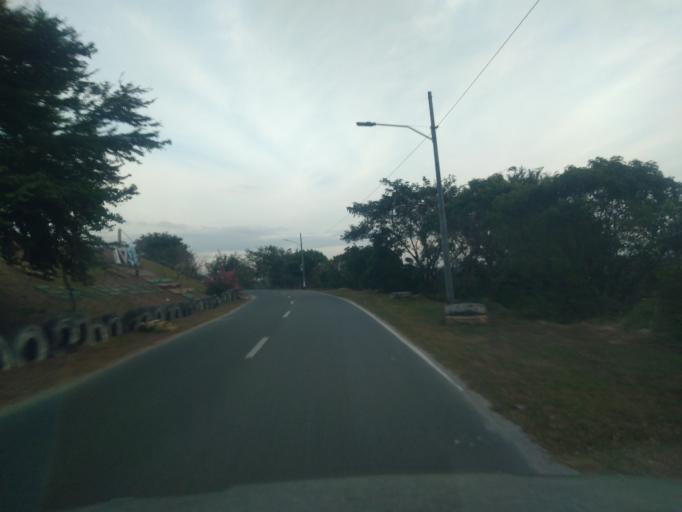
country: PH
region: Central Luzon
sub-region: Province of Pampanga
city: Santa Rita
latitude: 15.0192
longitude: 120.6039
